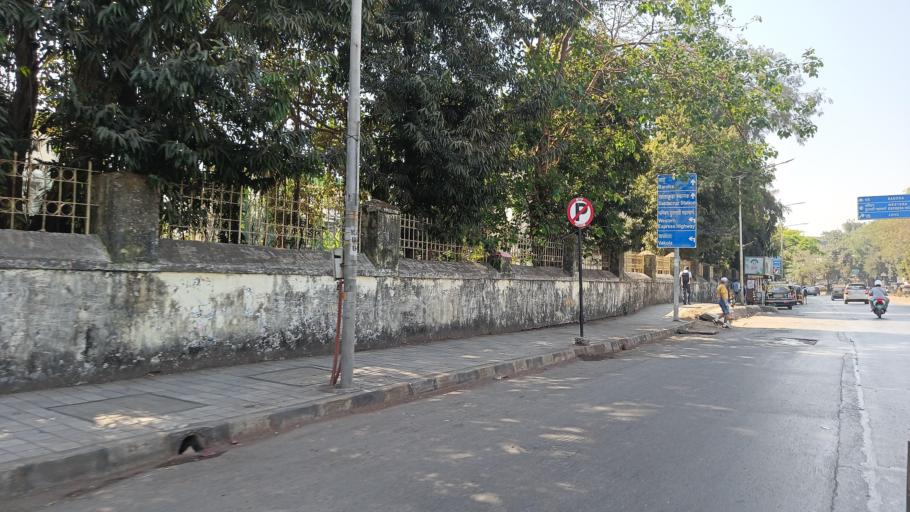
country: IN
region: Maharashtra
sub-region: Mumbai Suburban
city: Mumbai
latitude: 19.0925
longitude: 72.8390
